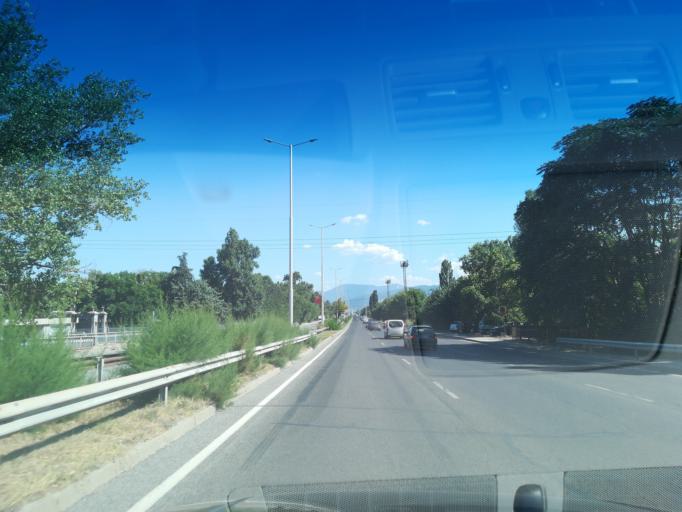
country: BG
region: Plovdiv
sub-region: Obshtina Plovdiv
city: Plovdiv
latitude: 42.1132
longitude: 24.7792
